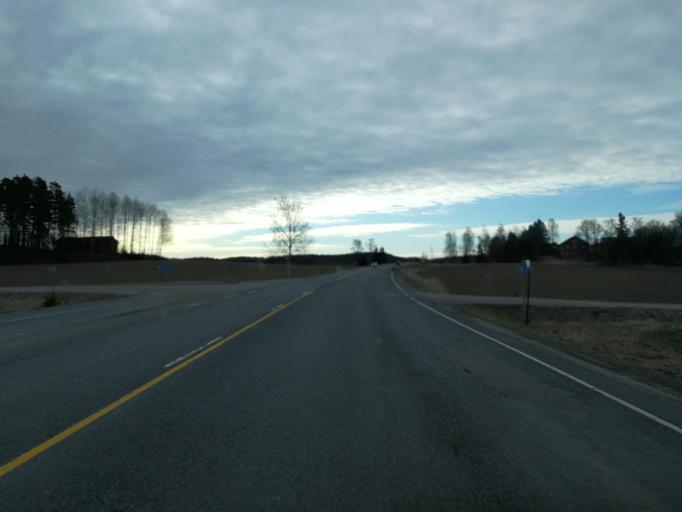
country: FI
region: Varsinais-Suomi
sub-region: Salo
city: Muurla
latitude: 60.3833
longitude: 23.2895
